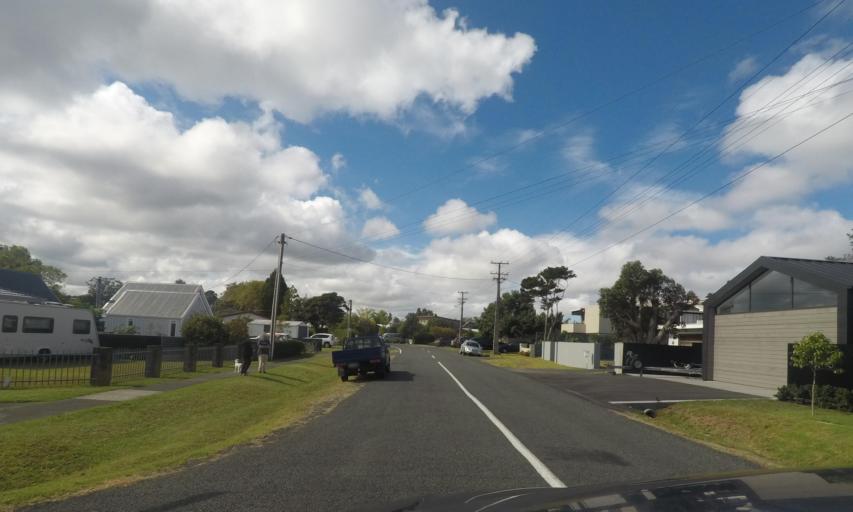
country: NZ
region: Auckland
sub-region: Auckland
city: North Shore
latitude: -36.7790
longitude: 174.6601
